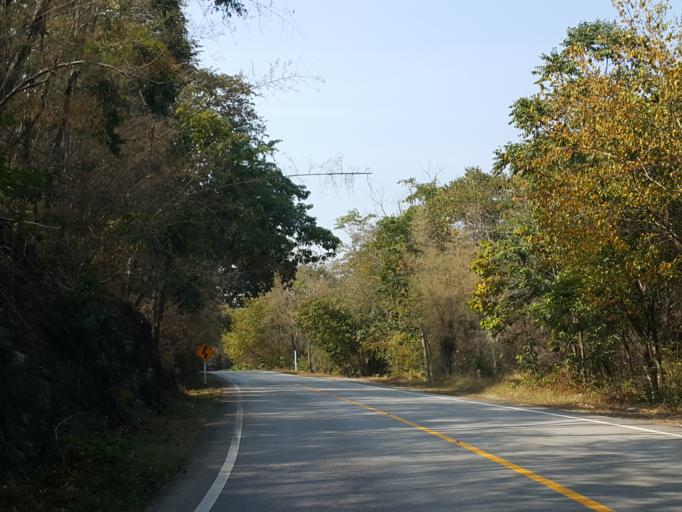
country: TH
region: Chiang Mai
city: Hot
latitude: 18.2299
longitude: 98.5128
